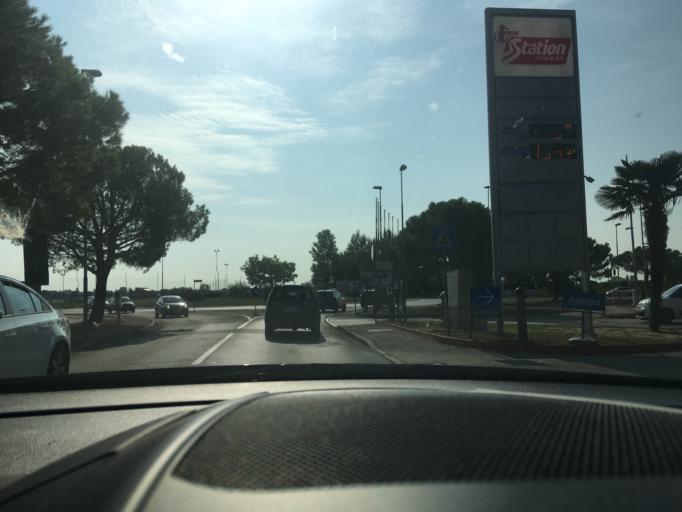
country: IT
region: Emilia-Romagna
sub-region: Forli-Cesena
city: Gatteo a Mare
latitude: 44.1563
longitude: 12.4330
